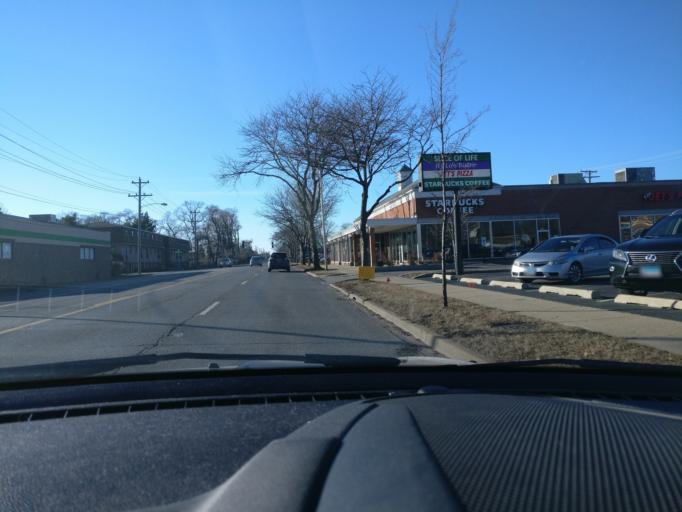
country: US
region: Illinois
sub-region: Cook County
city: Skokie
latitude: 42.0409
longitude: -87.7304
